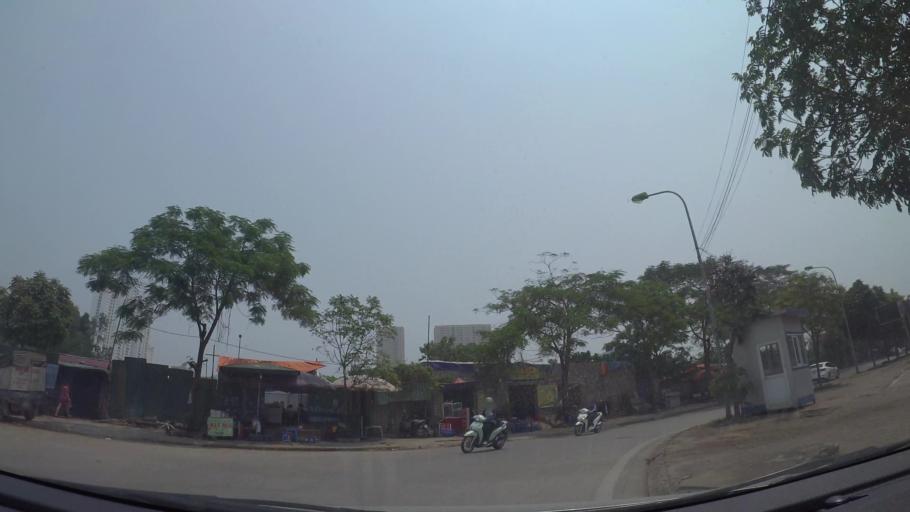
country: VN
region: Ha Noi
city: Thanh Xuan
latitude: 20.9947
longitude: 105.7813
